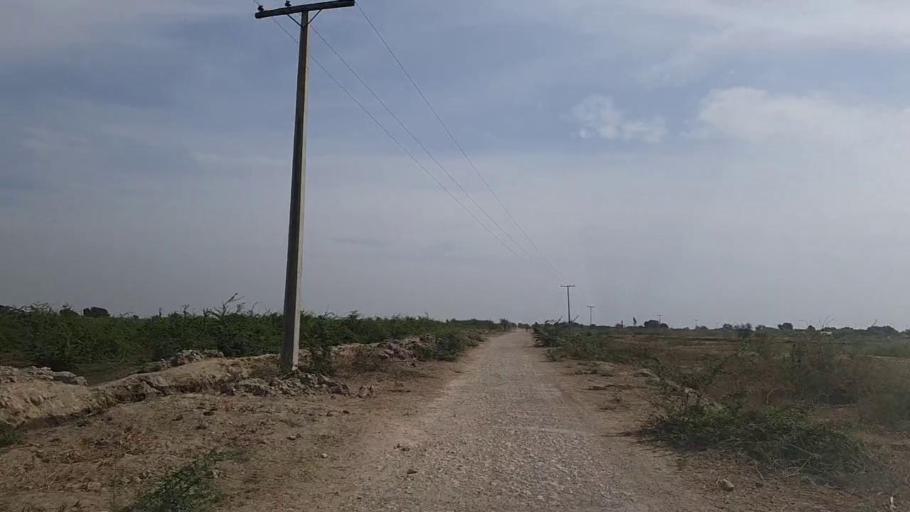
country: PK
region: Sindh
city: Samaro
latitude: 25.2056
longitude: 69.4604
